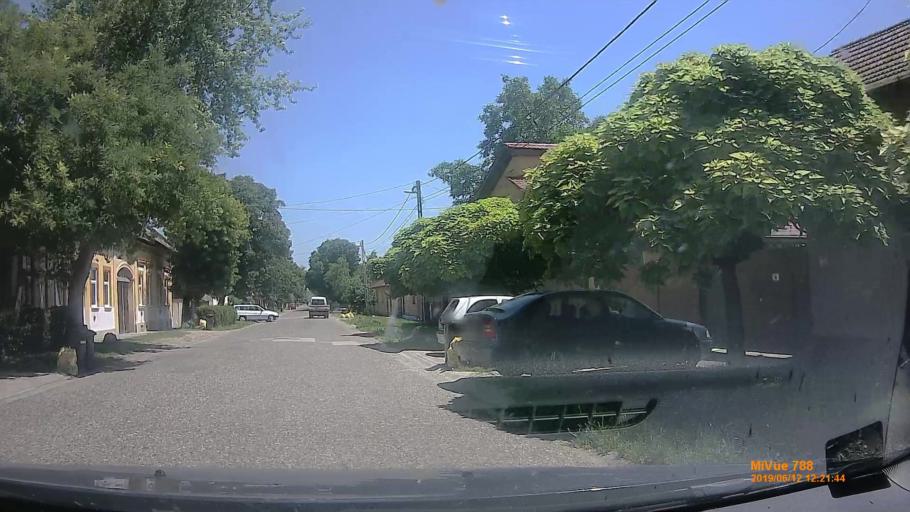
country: HU
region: Bacs-Kiskun
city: Kecskemet
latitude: 46.8969
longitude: 19.6941
